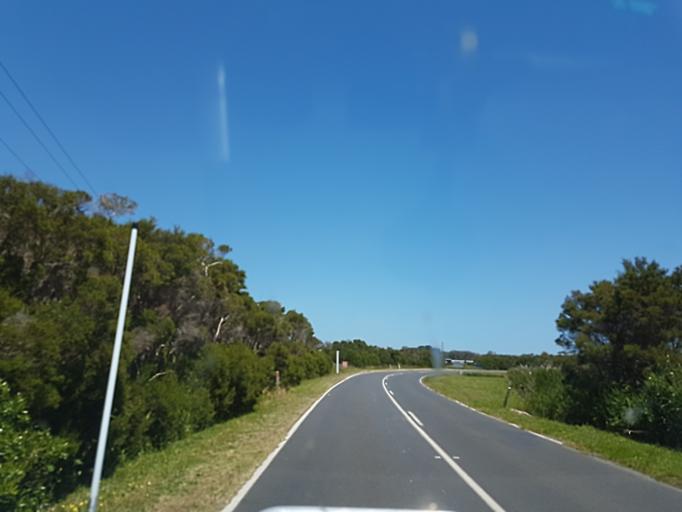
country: AU
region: Victoria
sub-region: Bass Coast
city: North Wonthaggi
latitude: -38.6986
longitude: 145.8781
